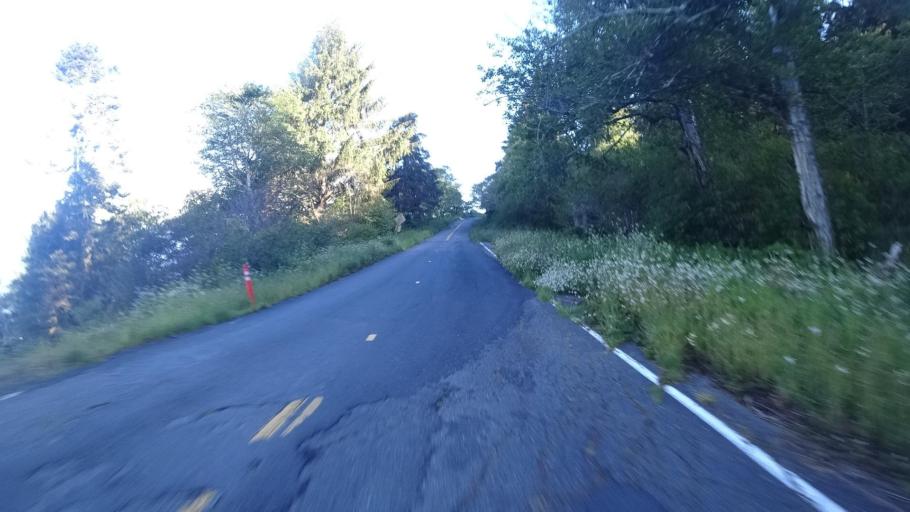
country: US
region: California
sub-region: Humboldt County
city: Westhaven-Moonstone
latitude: 41.1047
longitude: -124.1590
